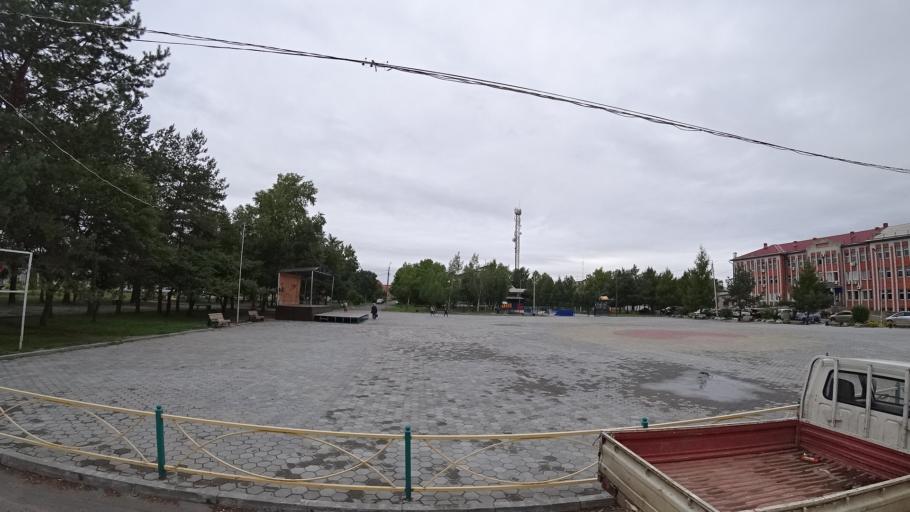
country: RU
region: Primorskiy
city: Chernigovka
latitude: 44.3434
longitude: 132.5759
